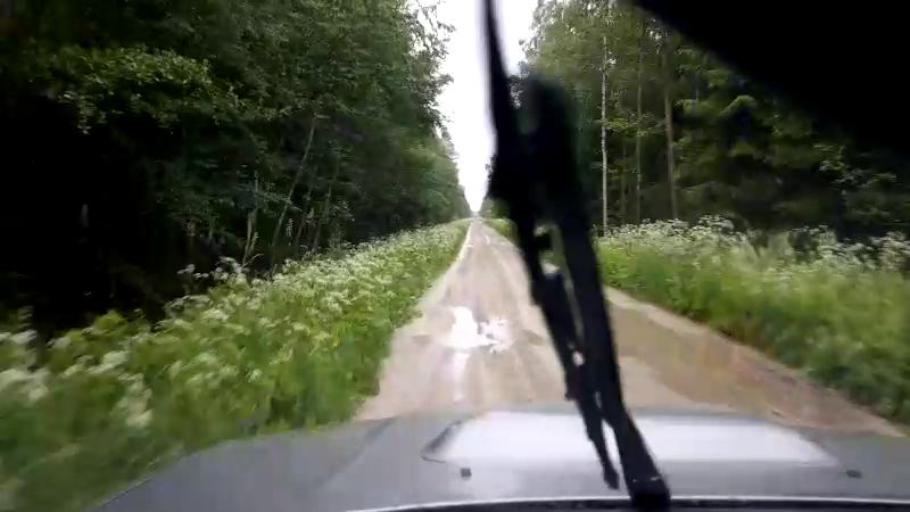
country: EE
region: Paernumaa
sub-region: Halinga vald
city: Parnu-Jaagupi
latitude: 58.5828
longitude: 24.6372
